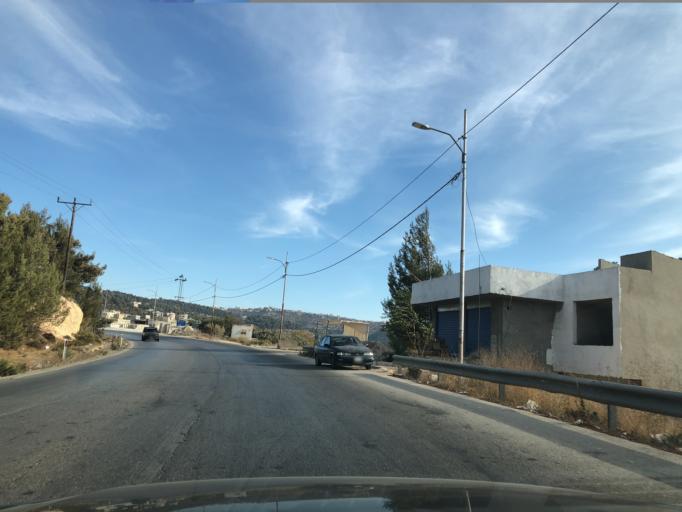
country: JO
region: Irbid
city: Sakib
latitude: 32.2807
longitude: 35.7952
